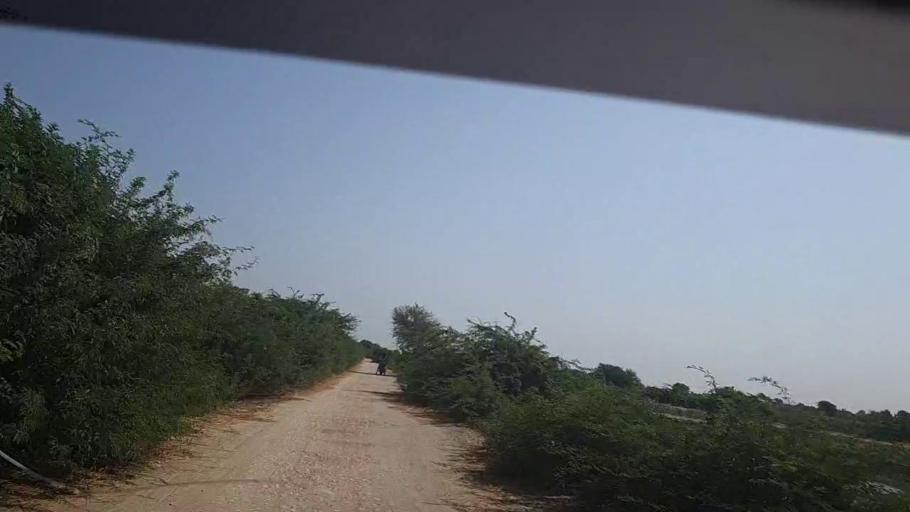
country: PK
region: Sindh
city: Rajo Khanani
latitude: 24.9876
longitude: 68.8643
